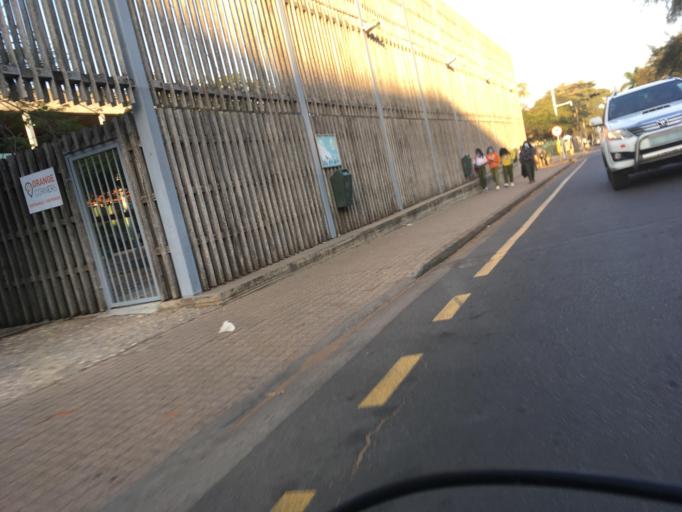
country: MZ
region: Maputo City
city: Maputo
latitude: -25.9655
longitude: 32.5954
